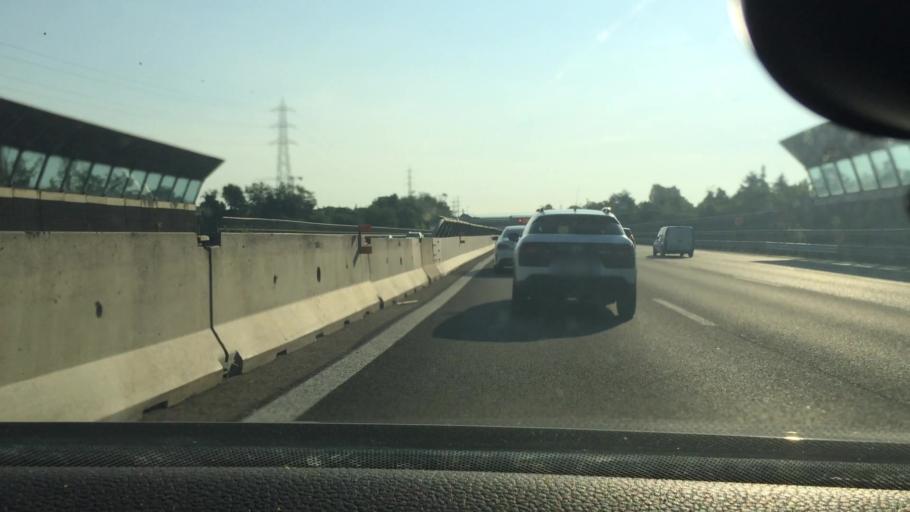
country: IT
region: Lombardy
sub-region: Provincia di Bergamo
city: Capriate San Gervasio
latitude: 45.6044
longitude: 9.5265
